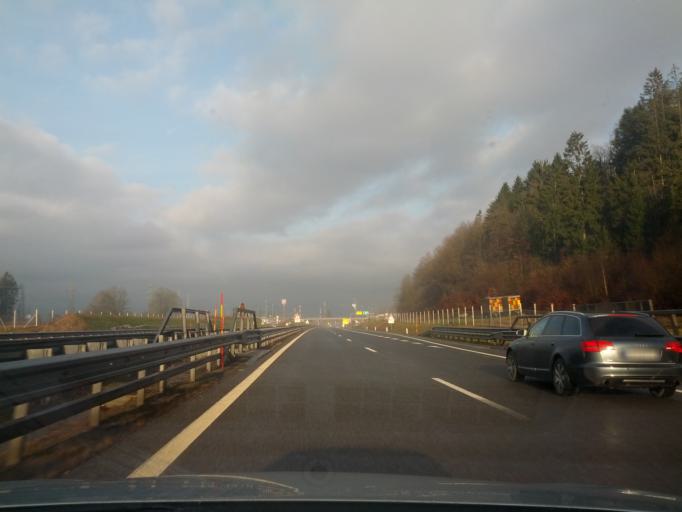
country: SI
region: Radovljica
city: Radovljica
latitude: 46.3353
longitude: 14.1968
